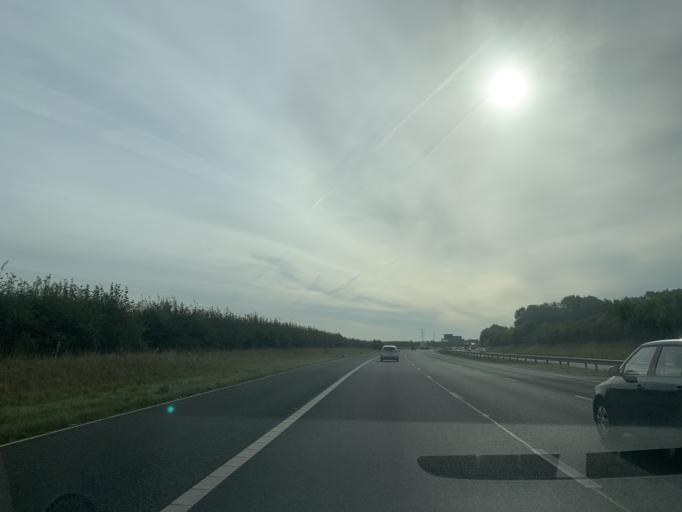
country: GB
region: England
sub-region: City and Borough of Leeds
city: Ledsham
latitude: 53.7768
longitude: -1.2967
